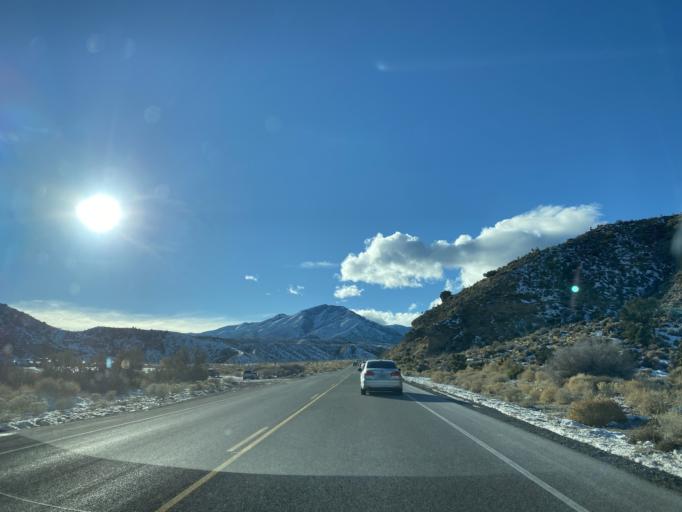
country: US
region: Nevada
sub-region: Clark County
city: Summerlin South
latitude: 36.2746
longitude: -115.5202
